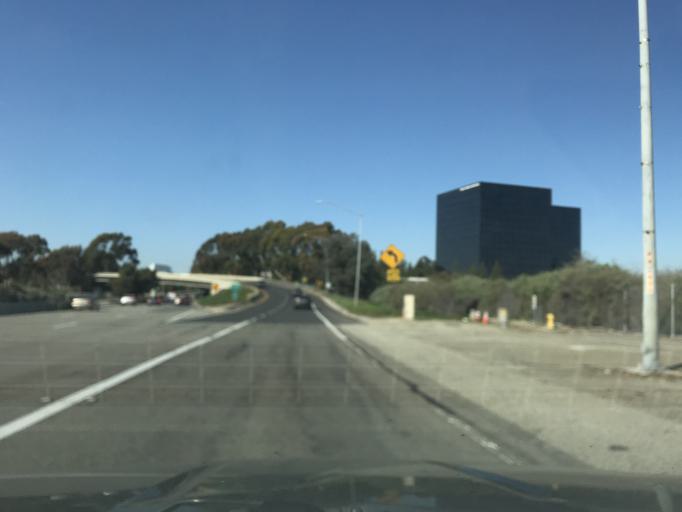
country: US
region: California
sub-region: Orange County
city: Irvine
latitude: 33.6522
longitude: -117.8602
